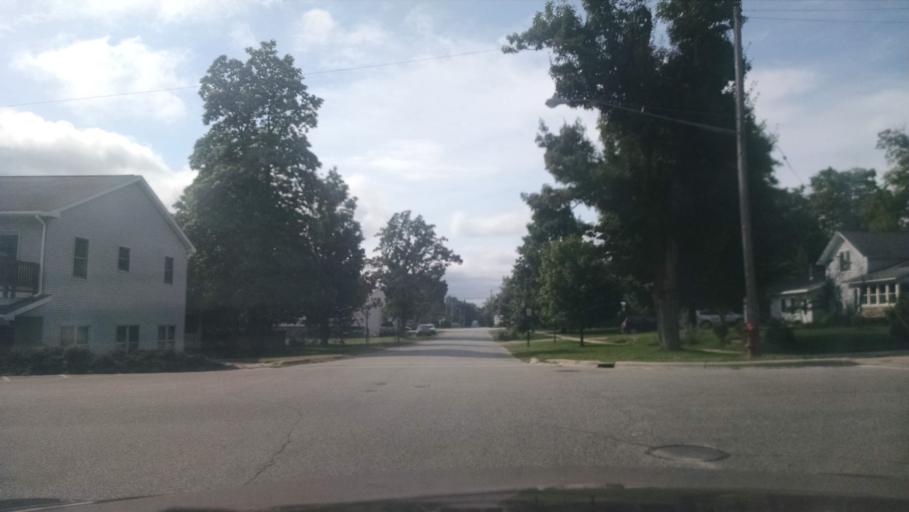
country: US
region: Michigan
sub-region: Leelanau County
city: Leland
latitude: 44.9758
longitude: -85.6525
